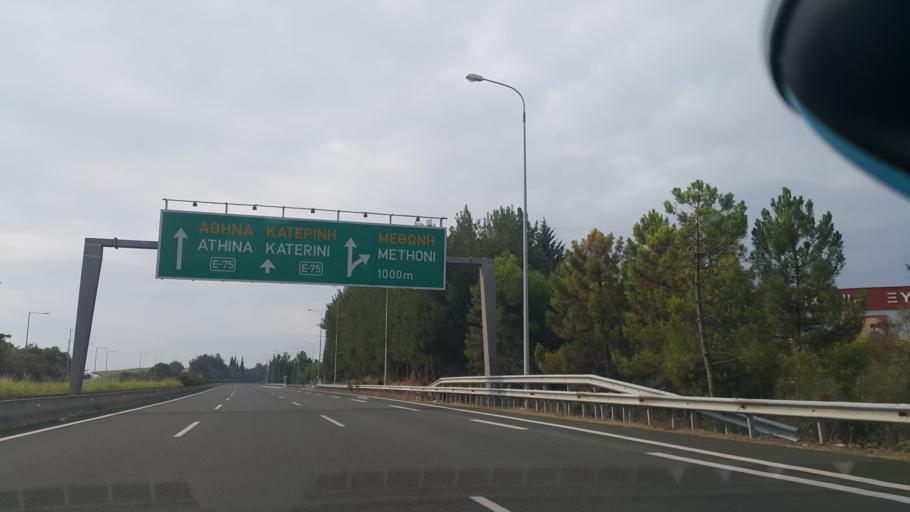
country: GR
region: Central Macedonia
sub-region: Nomos Pierias
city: Aiginio
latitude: 40.4712
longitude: 22.5729
